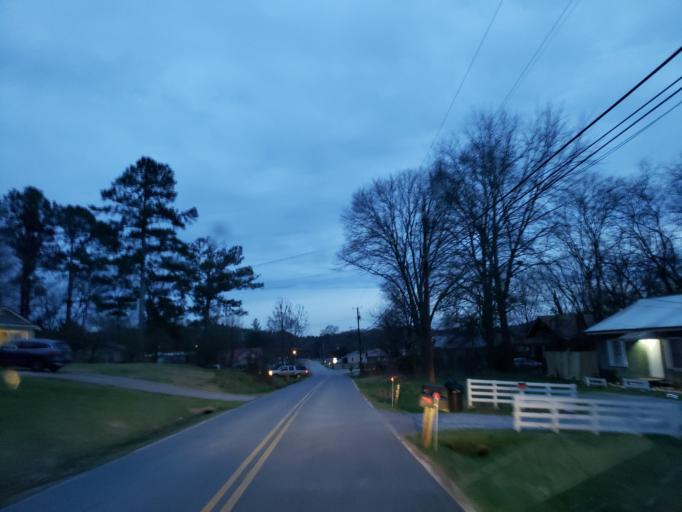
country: US
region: Georgia
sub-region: Bartow County
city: Emerson
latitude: 34.1285
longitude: -84.7555
